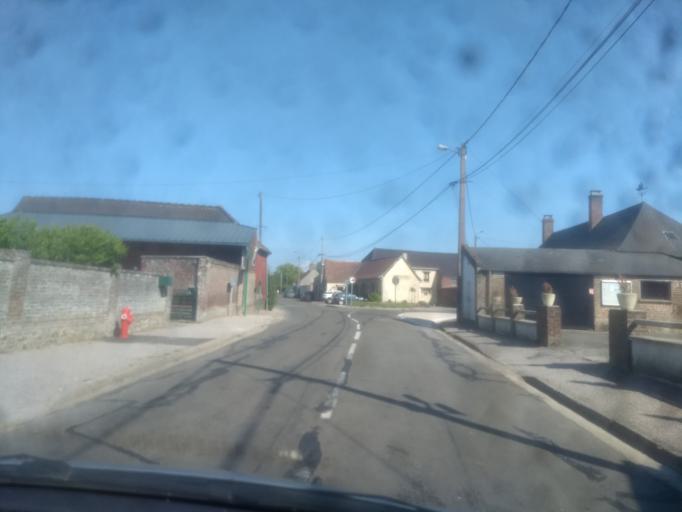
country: FR
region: Picardie
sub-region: Departement de la Somme
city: Nouvion
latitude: 50.1881
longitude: 1.8316
